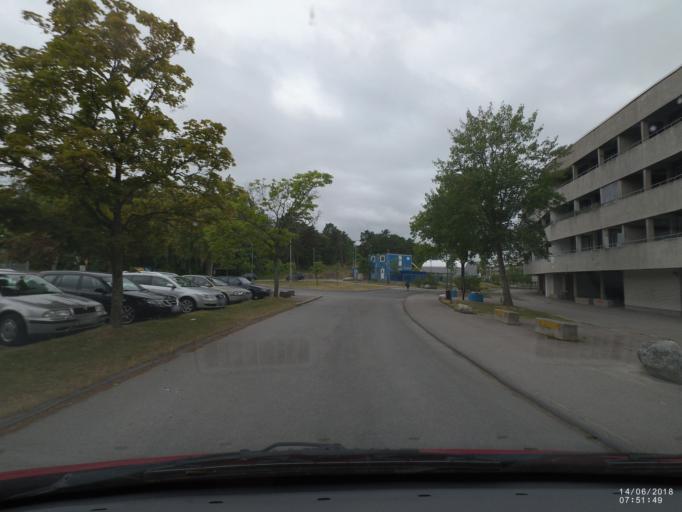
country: SE
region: Soedermanland
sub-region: Nykopings Kommun
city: Nykoping
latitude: 58.7650
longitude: 17.0226
